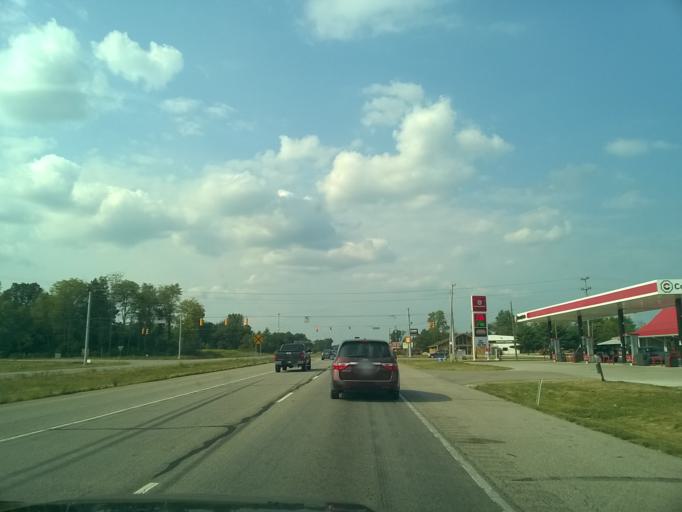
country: US
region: Indiana
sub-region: Sullivan County
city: Farmersburg
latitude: 39.3473
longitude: -87.3882
